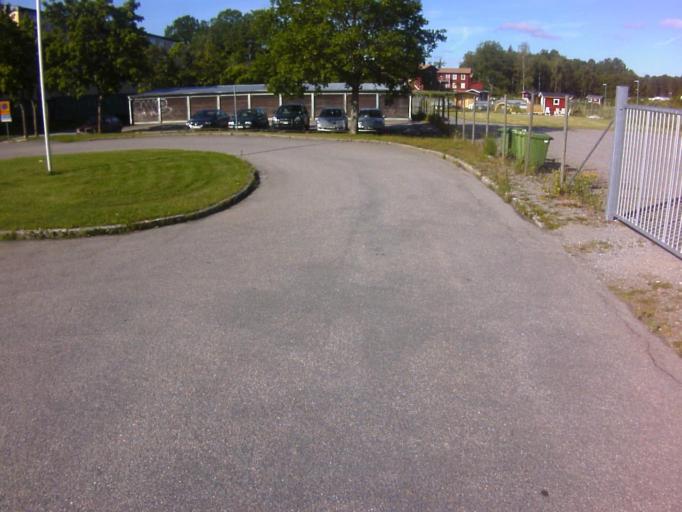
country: SE
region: Soedermanland
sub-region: Eskilstuna Kommun
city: Eskilstuna
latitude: 59.3587
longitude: 16.4830
